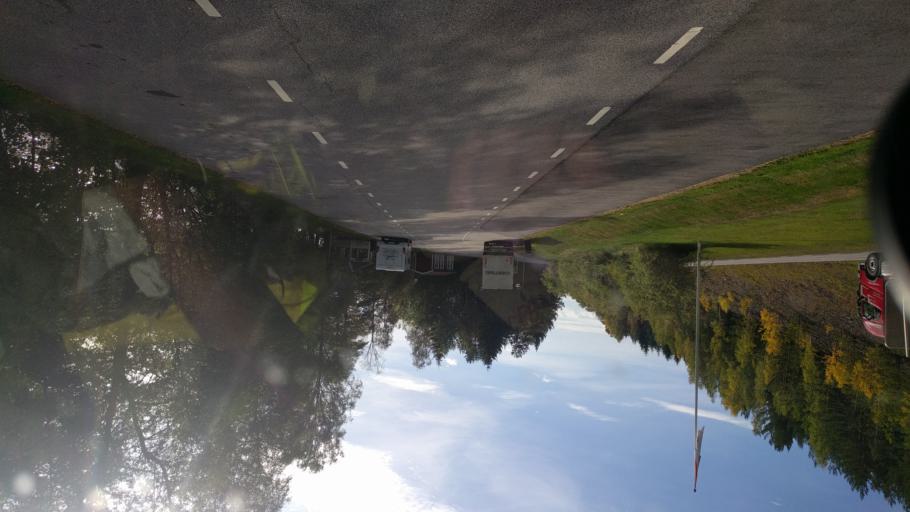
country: SE
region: OEstergoetland
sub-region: Kinda Kommun
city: Kisa
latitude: 57.9343
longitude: 15.6687
